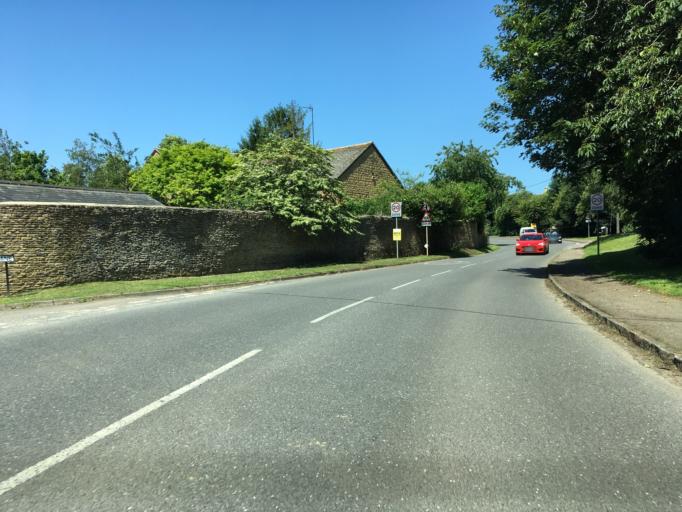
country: GB
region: England
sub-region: Northamptonshire
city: Brackley
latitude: 51.9977
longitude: -1.2046
